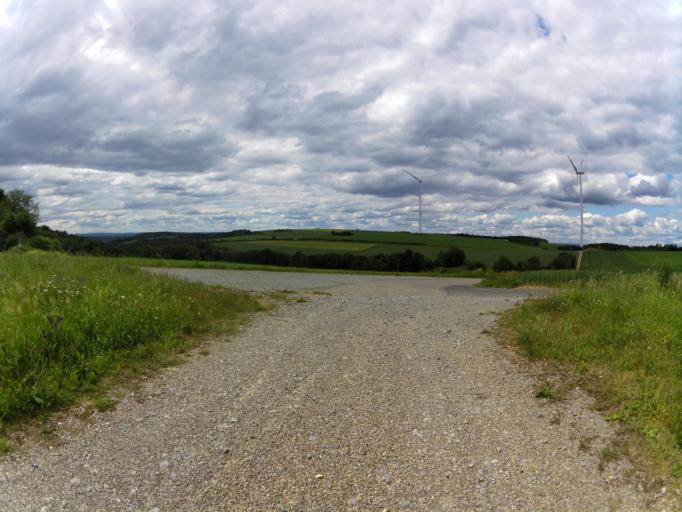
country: DE
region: Bavaria
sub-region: Regierungsbezirk Unterfranken
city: Retzstadt
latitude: 49.8876
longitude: 9.8835
